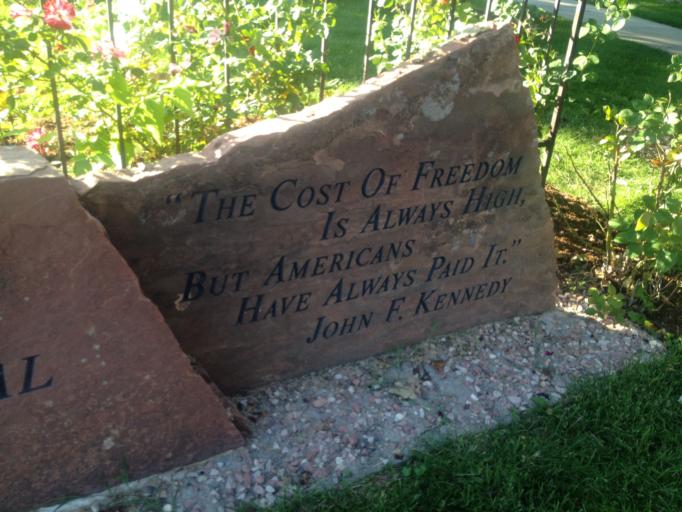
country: US
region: Colorado
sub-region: Boulder County
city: Longmont
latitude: 40.1723
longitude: -105.1080
